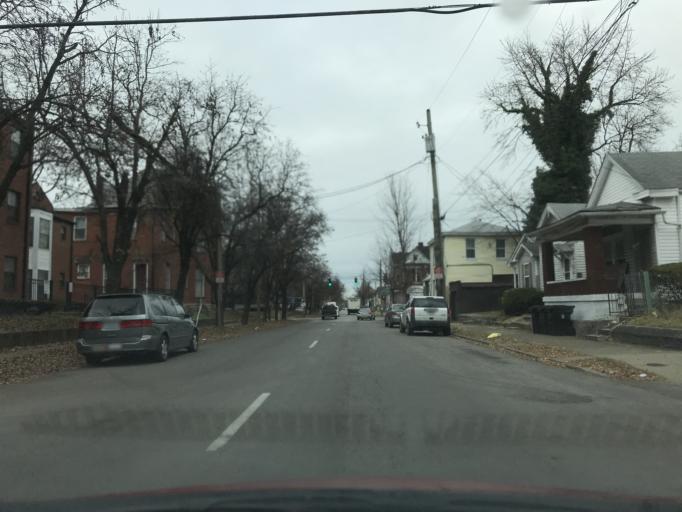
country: US
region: Kentucky
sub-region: Jefferson County
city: Louisville
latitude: 38.2514
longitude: -85.7861
